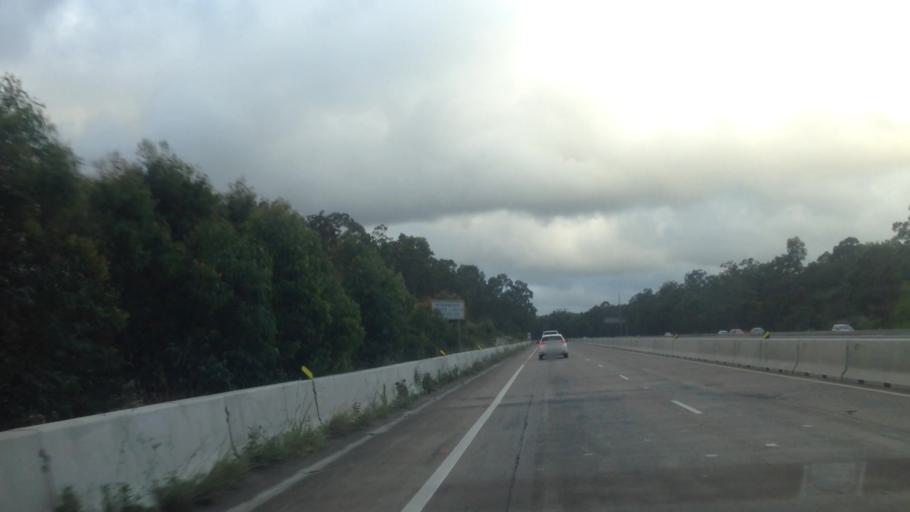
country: AU
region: New South Wales
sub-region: Wyong Shire
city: Jilliby
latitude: -33.2194
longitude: 151.4398
